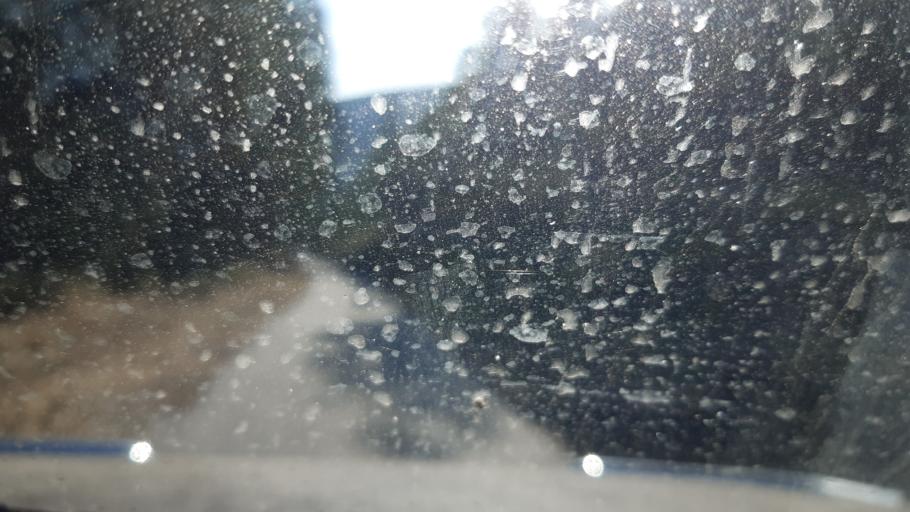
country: PT
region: Viseu
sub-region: Mortagua
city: Mortagua
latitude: 40.5326
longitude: -8.2477
